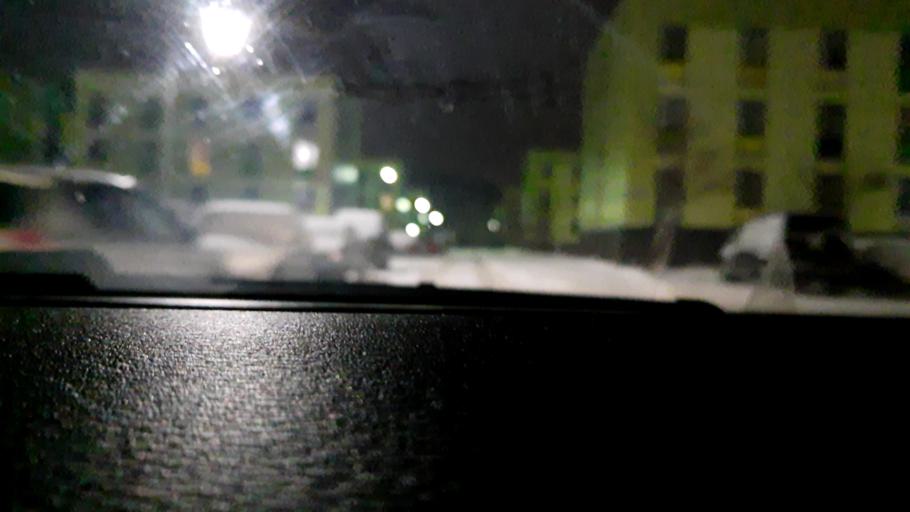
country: RU
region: Nizjnij Novgorod
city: Afonino
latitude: 56.2140
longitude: 44.0204
